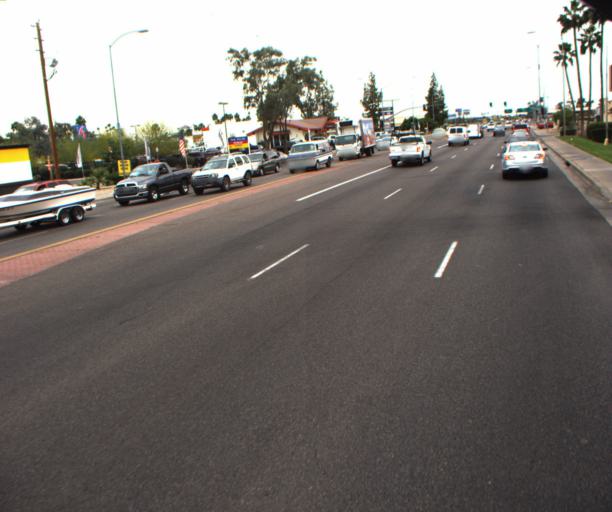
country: US
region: Arizona
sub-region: Maricopa County
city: Mesa
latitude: 33.3902
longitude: -111.8402
